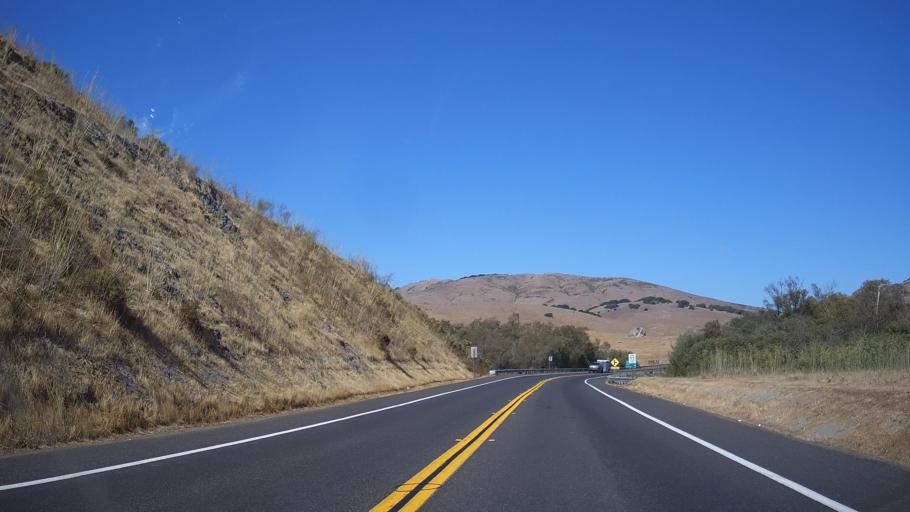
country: US
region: California
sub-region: Marin County
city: Lagunitas-Forest Knolls
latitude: 38.0953
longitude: -122.7350
